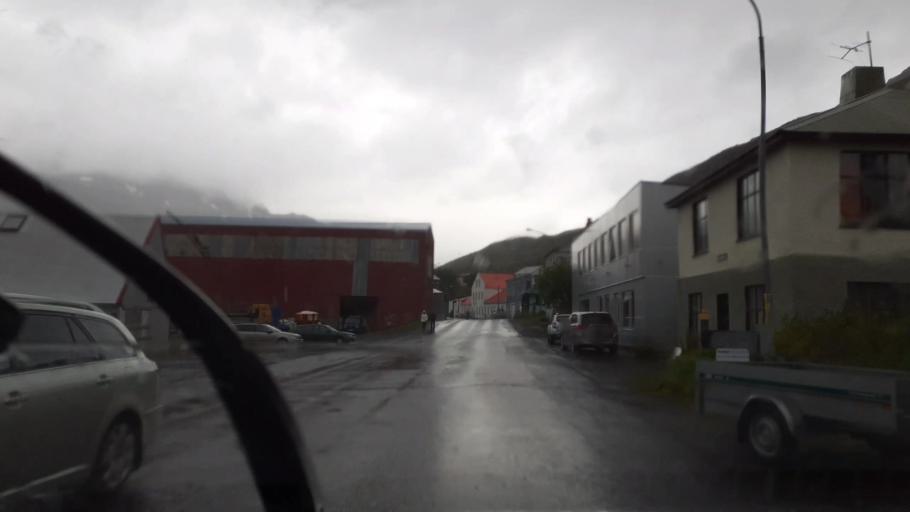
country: IS
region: East
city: Eskifjoerdur
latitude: 65.2644
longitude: -13.9942
